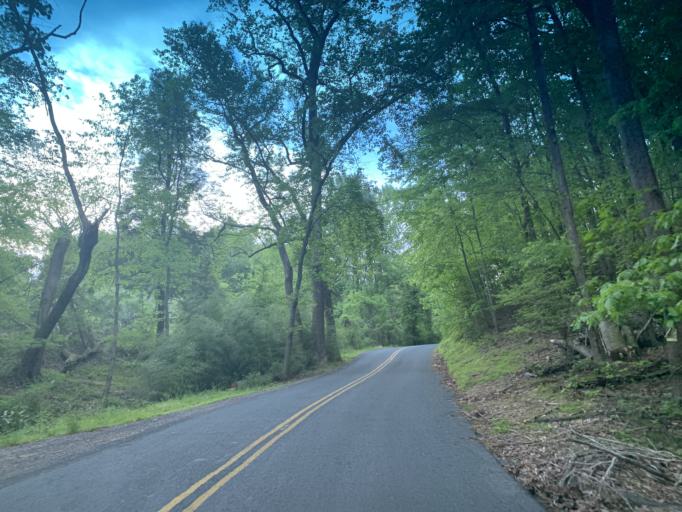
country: US
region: Pennsylvania
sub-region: York County
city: Susquehanna Trails
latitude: 39.6929
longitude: -76.2779
